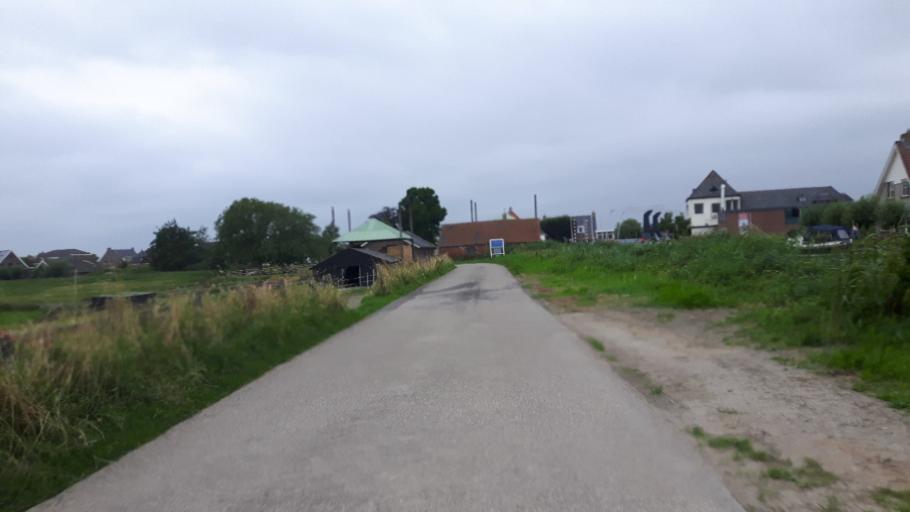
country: NL
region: South Holland
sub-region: Gemeente Kaag en Braassem
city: Leimuiden
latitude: 52.2207
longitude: 4.6741
